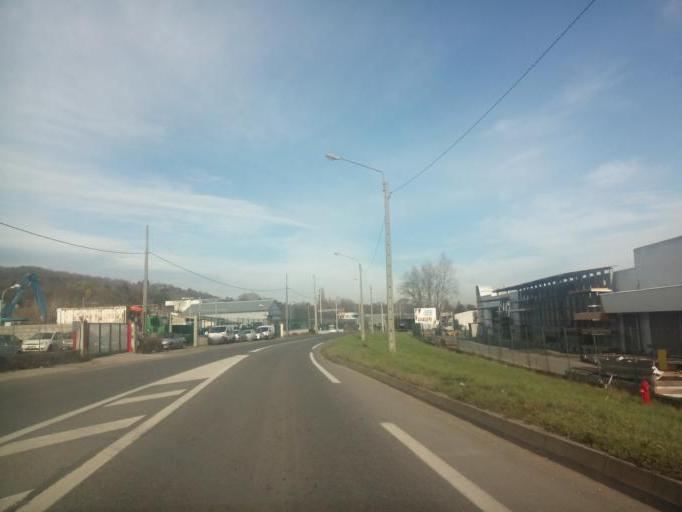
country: FR
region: Rhone-Alpes
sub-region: Departement du Rhone
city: Chaponost
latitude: 45.7052
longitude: 4.7679
